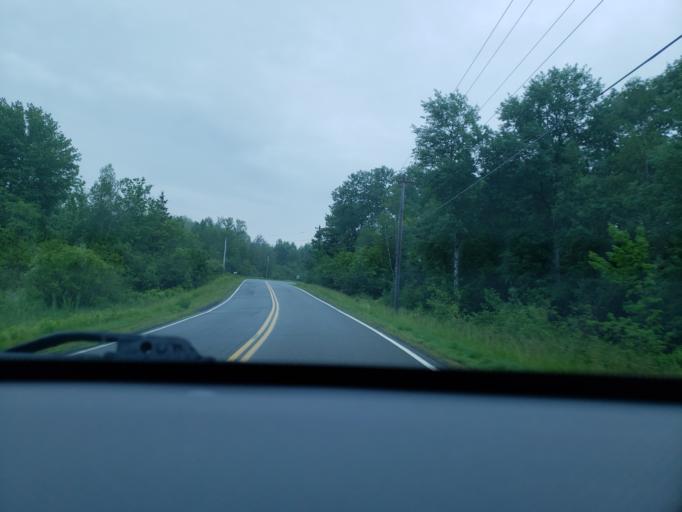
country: CA
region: Nova Scotia
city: Windsor
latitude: 45.0608
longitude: -63.9861
